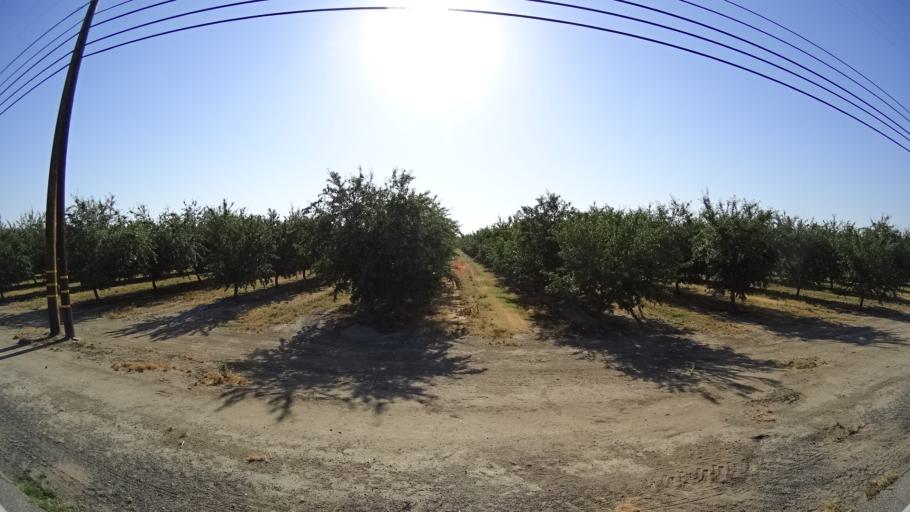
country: US
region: California
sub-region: Kings County
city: Armona
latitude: 36.3611
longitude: -119.7090
